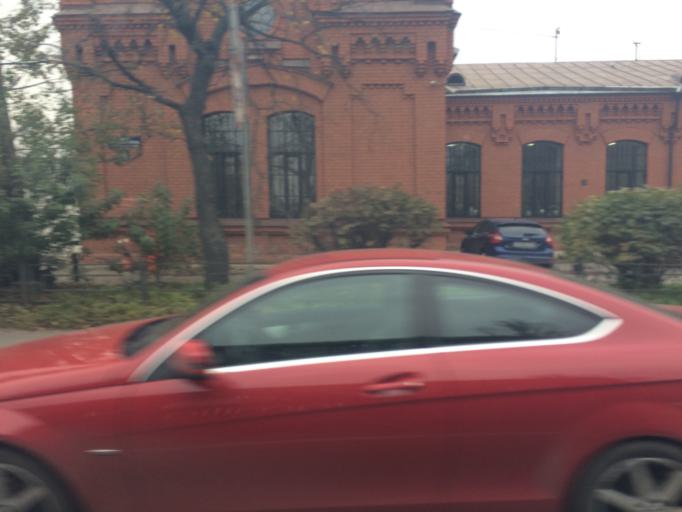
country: RU
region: Leningrad
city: Rybatskoye
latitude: 59.8600
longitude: 30.4789
